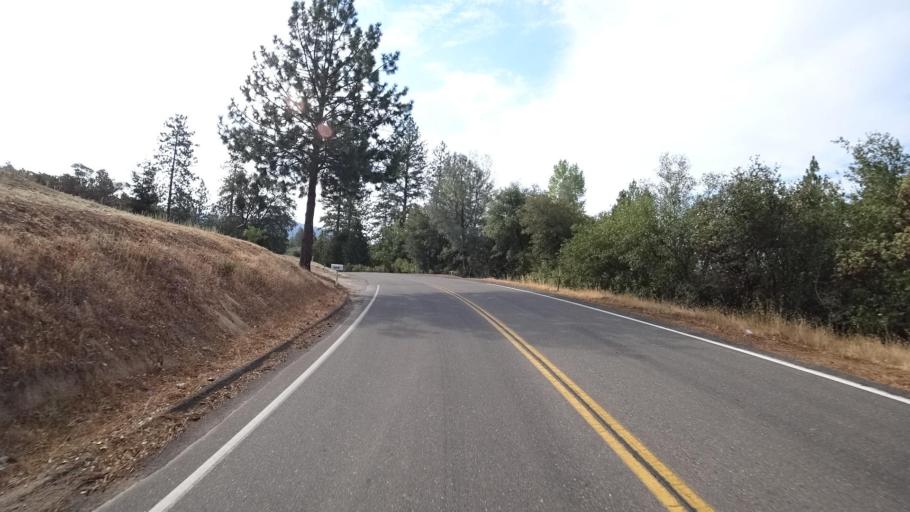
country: US
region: California
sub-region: Madera County
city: Ahwahnee
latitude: 37.4683
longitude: -119.7685
